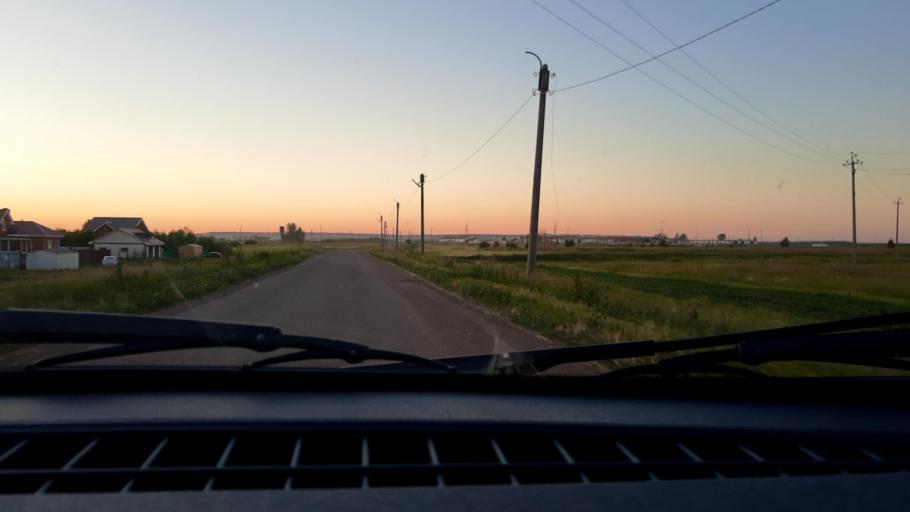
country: RU
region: Bashkortostan
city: Asanovo
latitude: 54.8920
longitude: 55.6248
